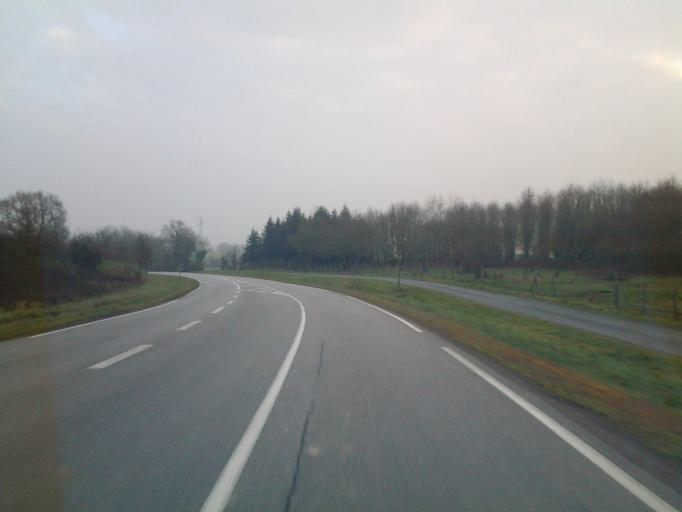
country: FR
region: Pays de la Loire
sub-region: Departement de la Vendee
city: Nesmy
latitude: 46.6263
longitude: -1.4063
